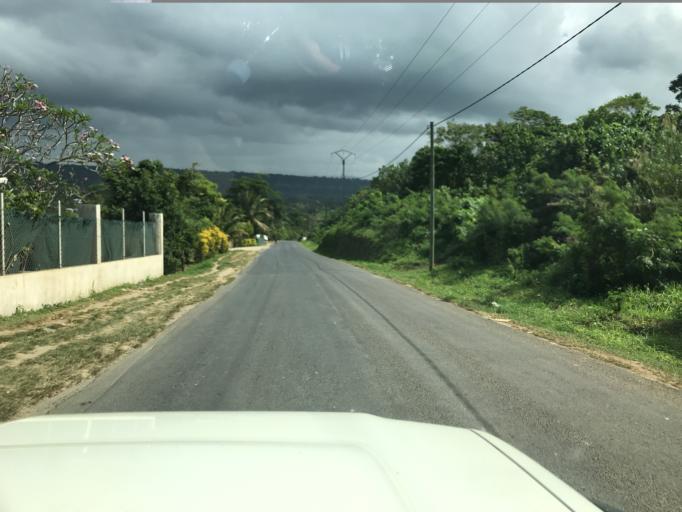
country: VU
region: Sanma
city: Luganville
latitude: -15.5104
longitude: 167.1814
